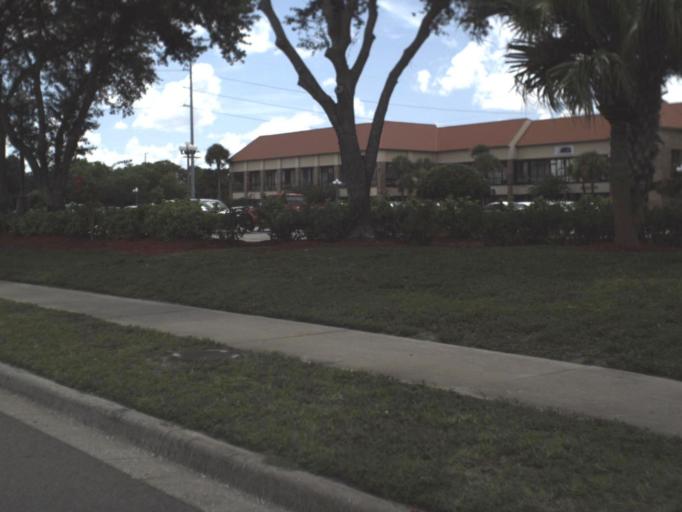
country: US
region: Florida
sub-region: Hillsborough County
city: Egypt Lake-Leto
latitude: 28.0087
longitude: -82.5052
